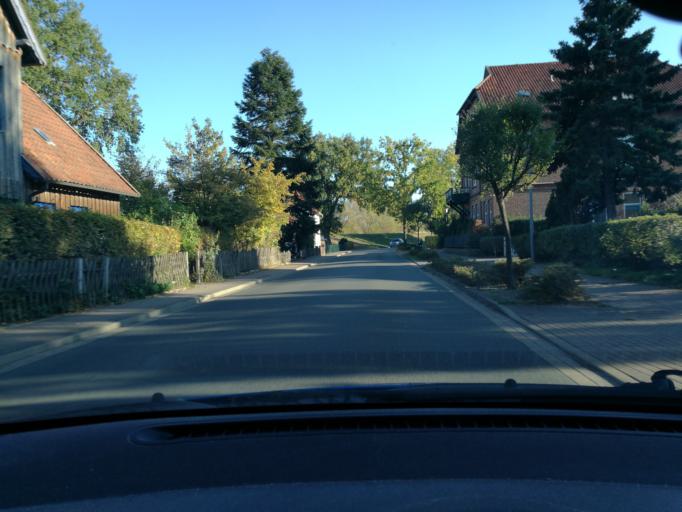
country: DE
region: Lower Saxony
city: Bleckede
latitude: 53.2883
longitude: 10.7376
